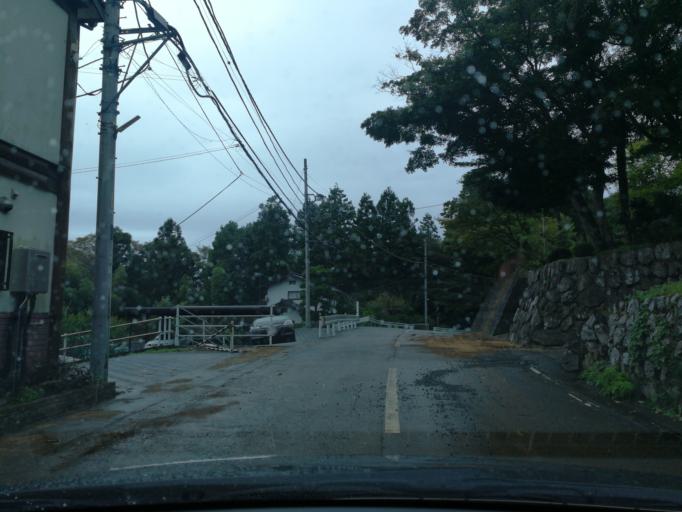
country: JP
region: Yamanashi
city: Uenohara
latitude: 35.6114
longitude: 139.2221
